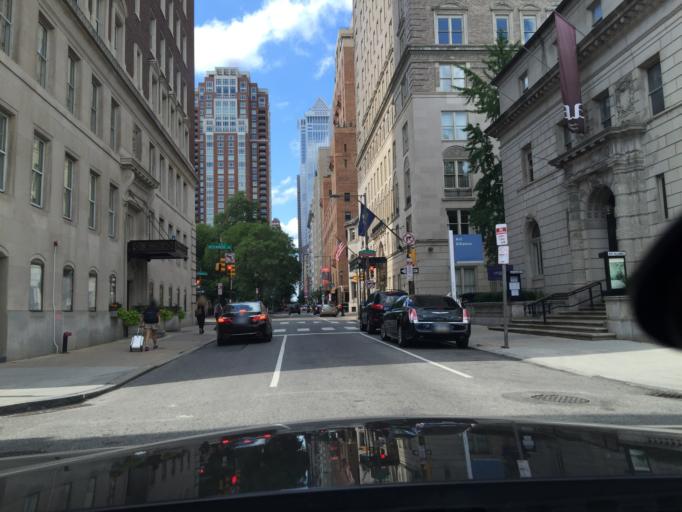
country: US
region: Pennsylvania
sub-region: Philadelphia County
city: Philadelphia
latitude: 39.9481
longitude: -75.1711
